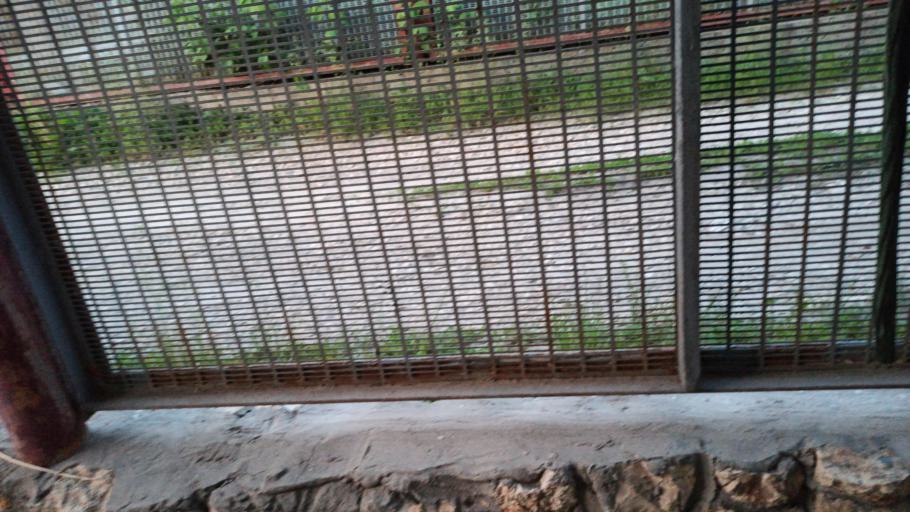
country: RU
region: Volgograd
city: Frolovo
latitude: 49.7701
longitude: 43.6712
